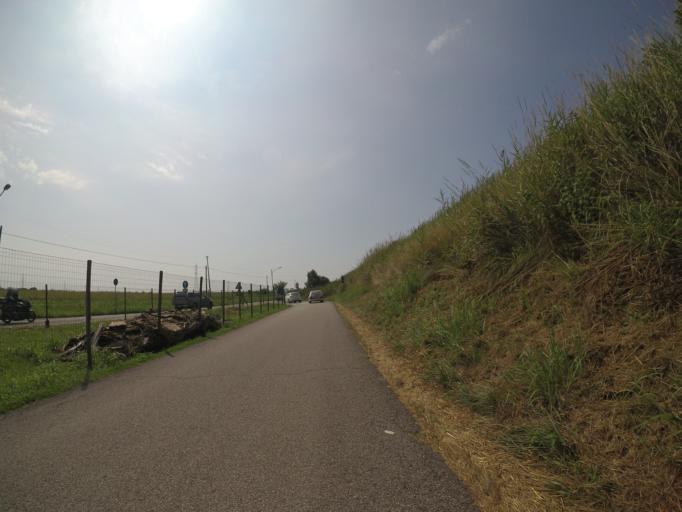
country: IT
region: Friuli Venezia Giulia
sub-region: Provincia di Udine
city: Pertegada
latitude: 45.6949
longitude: 13.0555
